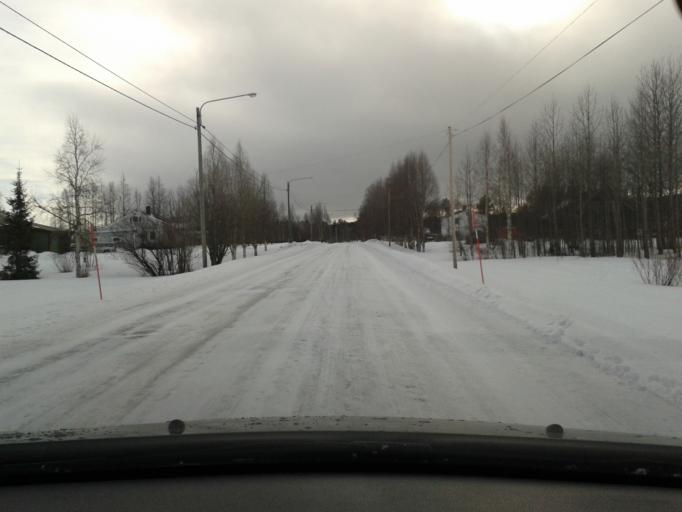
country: SE
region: Vaesterbotten
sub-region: Vilhelmina Kommun
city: Sjoberg
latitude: 64.6800
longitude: 16.2895
